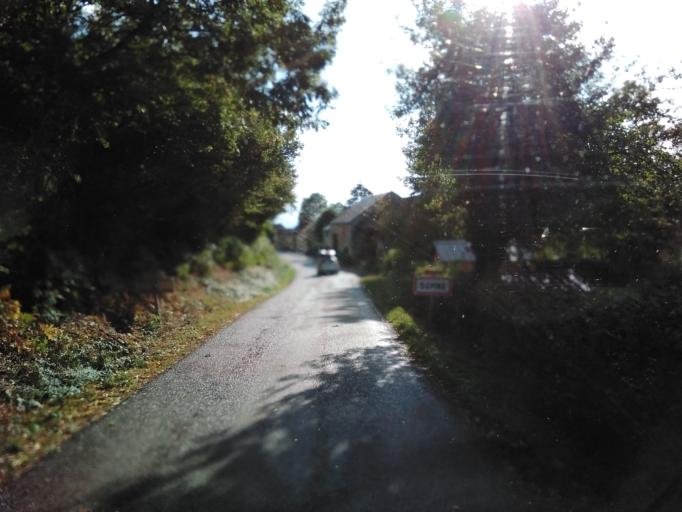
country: FR
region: Bourgogne
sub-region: Departement de la Nievre
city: Lormes
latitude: 47.2948
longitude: 3.8589
